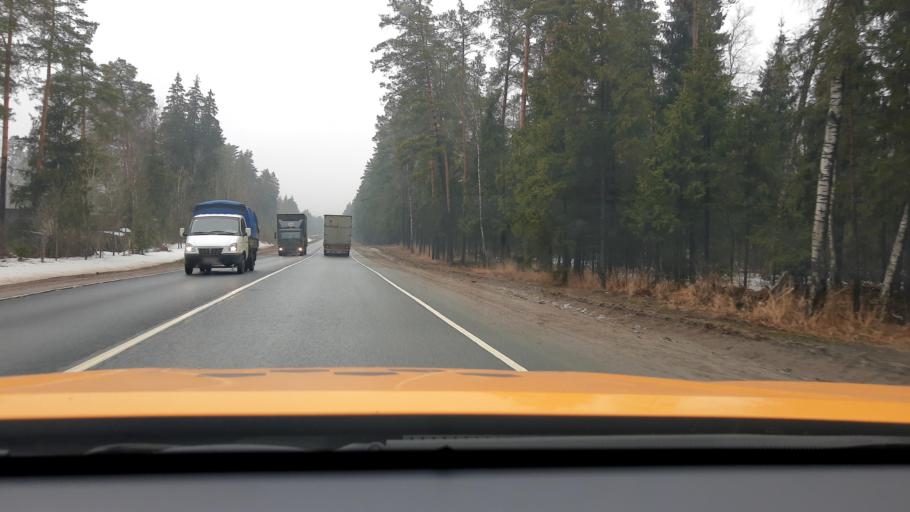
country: RU
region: Moskovskaya
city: Chernogolovka
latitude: 55.9896
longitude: 38.3300
